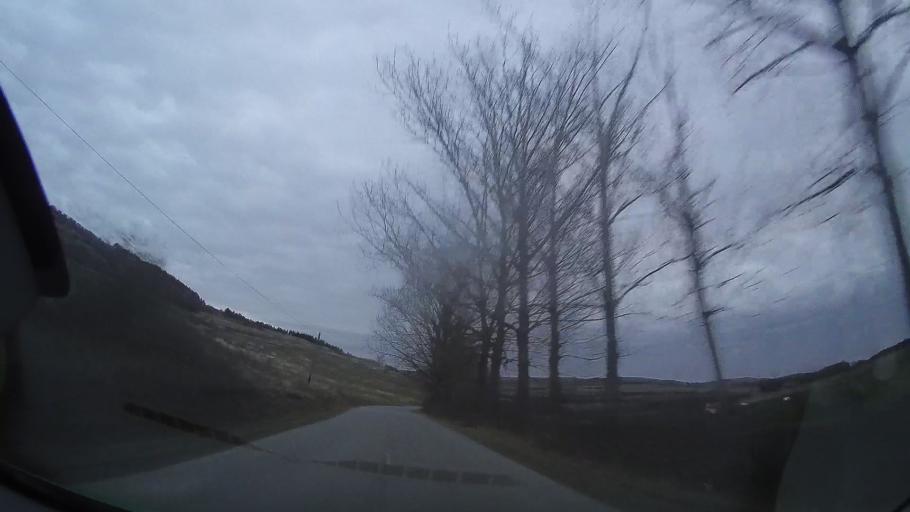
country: RO
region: Cluj
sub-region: Comuna Caianu
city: Caianu
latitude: 46.8073
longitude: 23.9294
